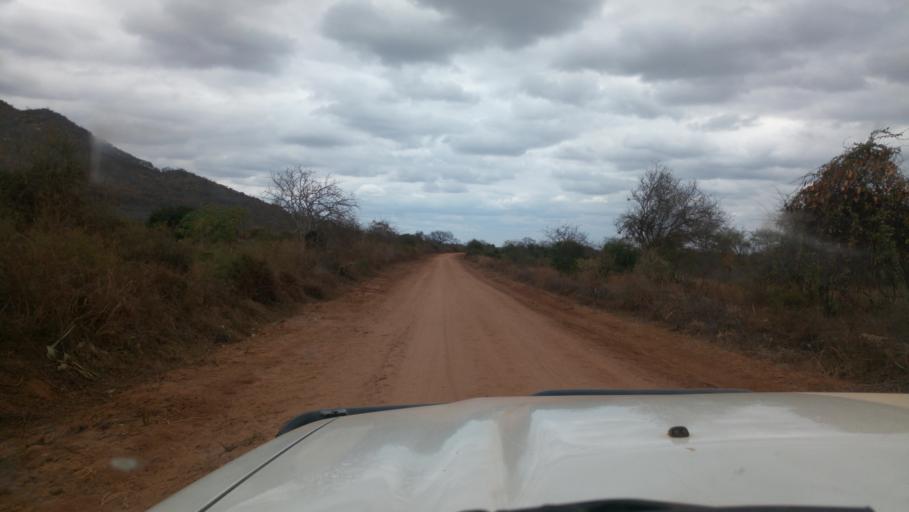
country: KE
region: Kitui
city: Kitui
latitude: -1.9381
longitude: 38.3753
